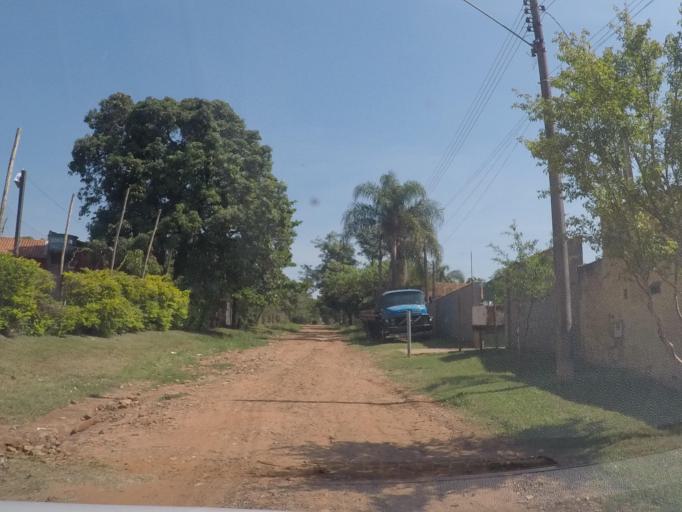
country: BR
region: Sao Paulo
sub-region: Sumare
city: Sumare
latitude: -22.8812
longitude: -47.2975
